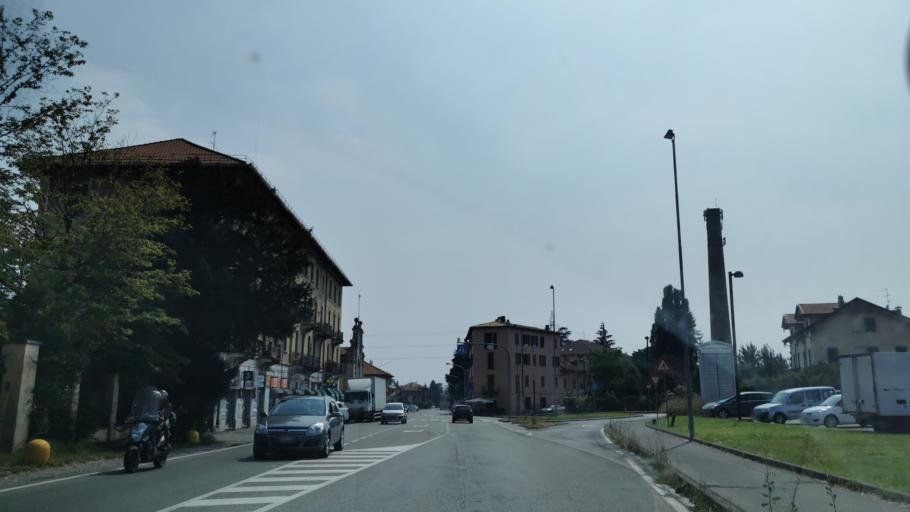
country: IT
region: Lombardy
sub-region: Provincia di Lecco
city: Cernusco Lombardone
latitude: 45.6973
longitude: 9.4054
